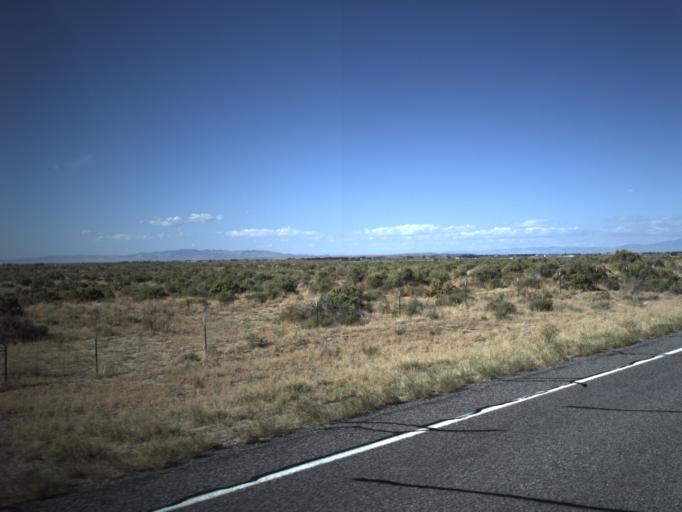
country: US
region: Utah
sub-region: Millard County
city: Delta
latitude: 39.3534
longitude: -112.4866
